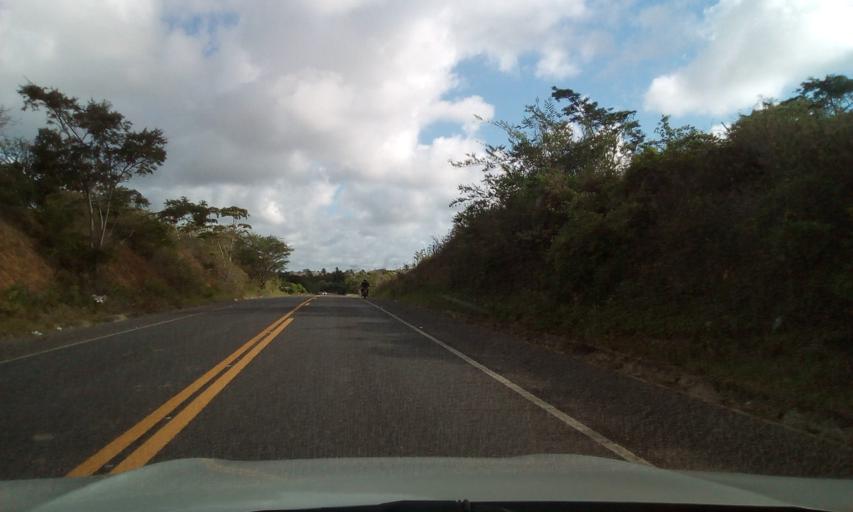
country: BR
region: Bahia
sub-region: Conde
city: Conde
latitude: -11.8037
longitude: -37.6294
